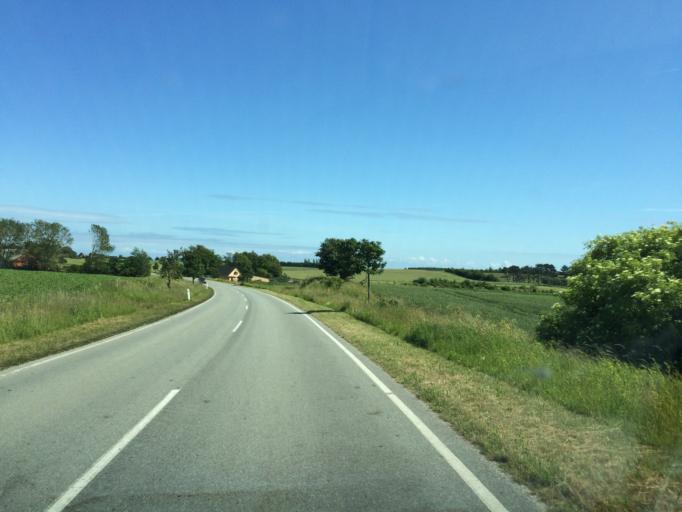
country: DK
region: Central Jutland
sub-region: Samso Kommune
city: Tranebjerg
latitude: 55.8126
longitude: 10.6190
